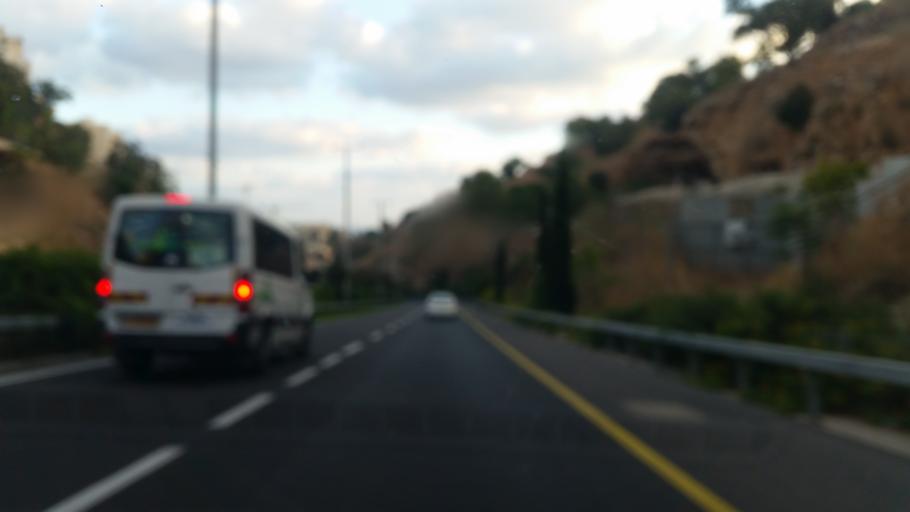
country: IL
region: Haifa
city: Haifa
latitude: 32.7965
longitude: 35.0048
